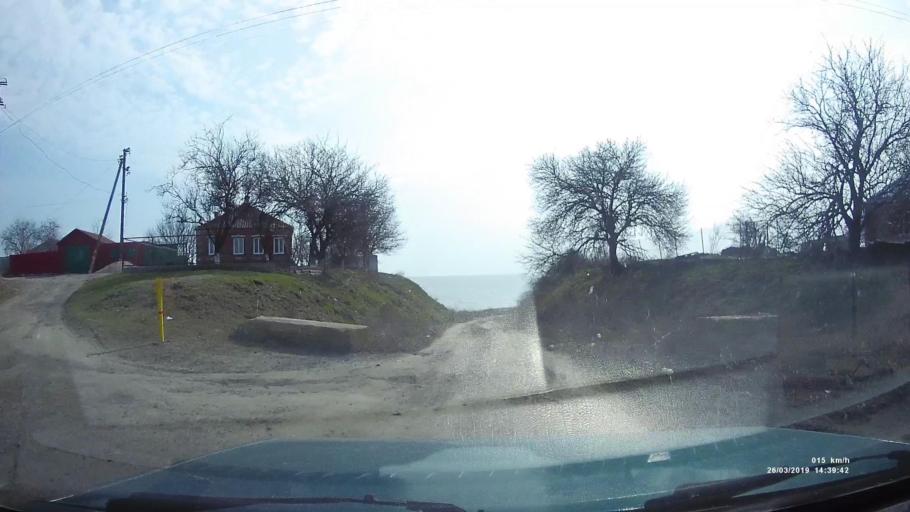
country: RU
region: Rostov
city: Novobessergenovka
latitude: 47.1775
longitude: 38.8626
